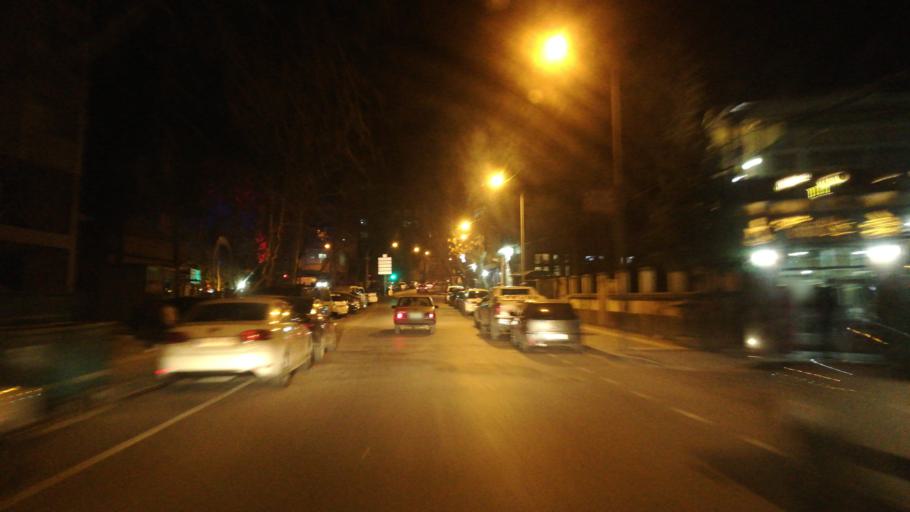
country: TR
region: Kahramanmaras
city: Kahramanmaras
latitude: 37.5894
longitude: 36.9298
